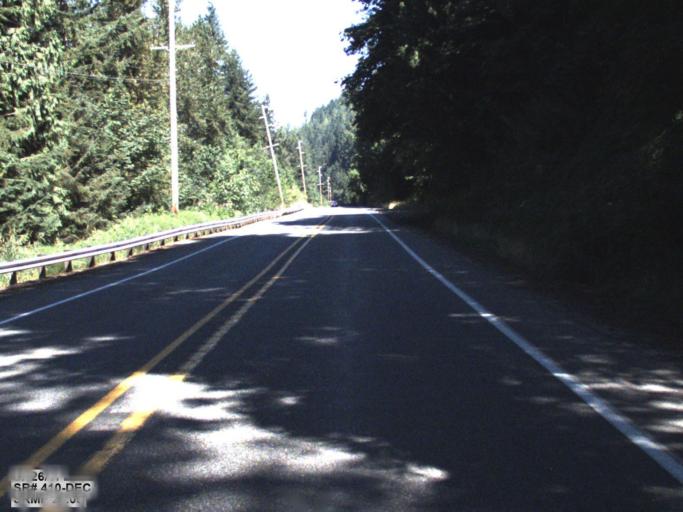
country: US
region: Washington
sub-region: King County
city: Enumclaw
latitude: 47.1697
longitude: -121.9134
